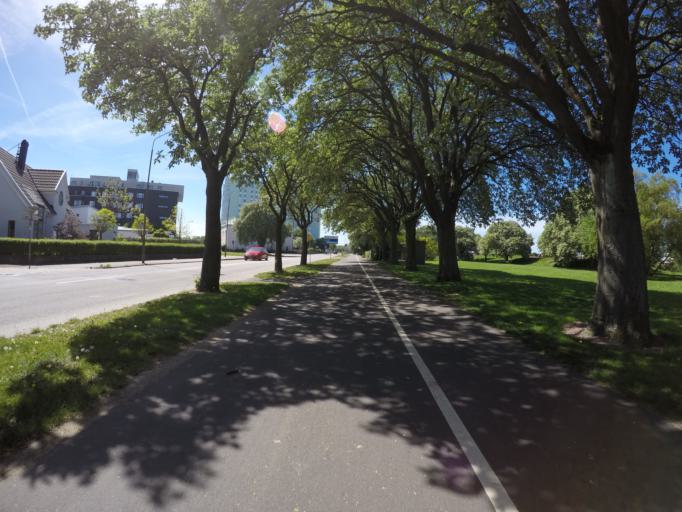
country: SE
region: Skane
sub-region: Malmo
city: Bunkeflostrand
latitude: 55.5837
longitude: 12.9230
